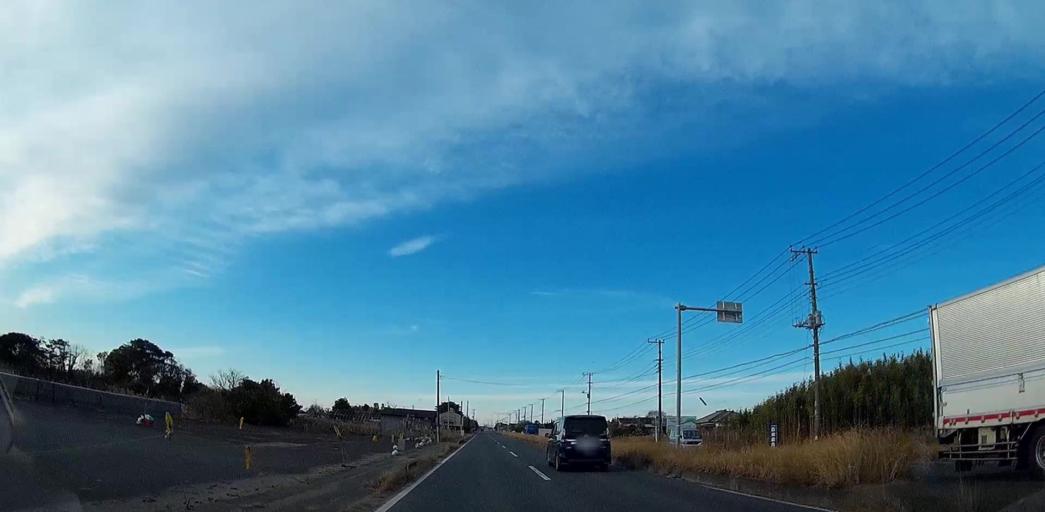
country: JP
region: Chiba
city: Hasaki
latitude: 35.7917
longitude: 140.7599
